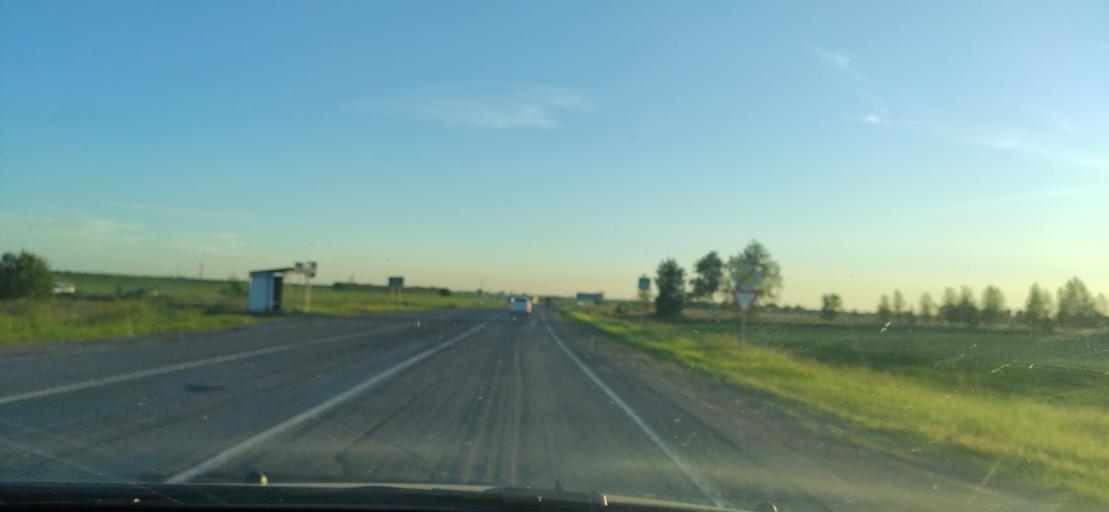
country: RU
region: Ulyanovsk
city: Mirnyy
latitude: 54.3753
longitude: 48.7862
